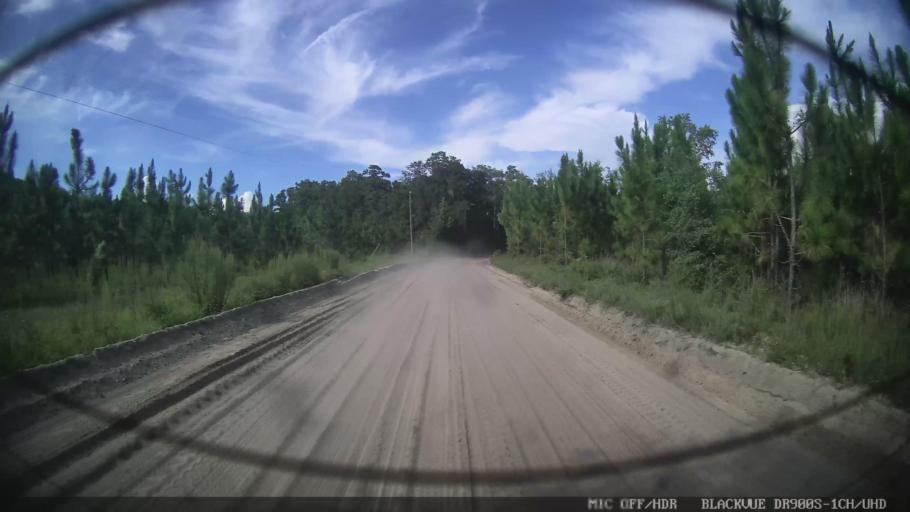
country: US
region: Georgia
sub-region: Echols County
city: Statenville
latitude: 30.6213
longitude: -83.2134
